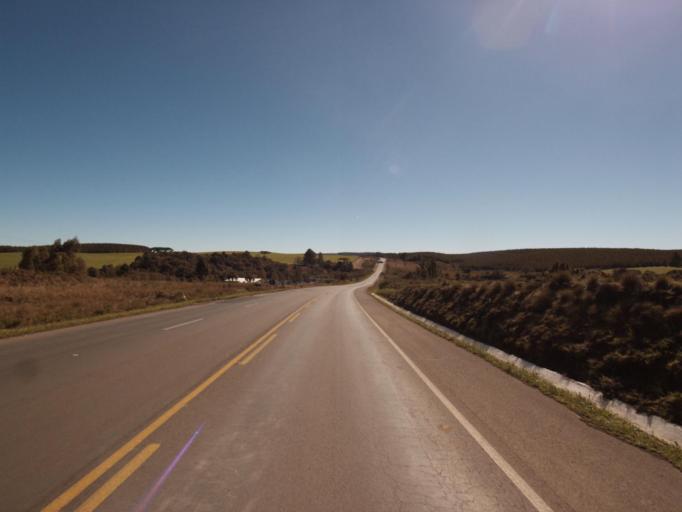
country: BR
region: Santa Catarina
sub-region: Concordia
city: Concordia
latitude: -26.9325
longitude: -51.8727
